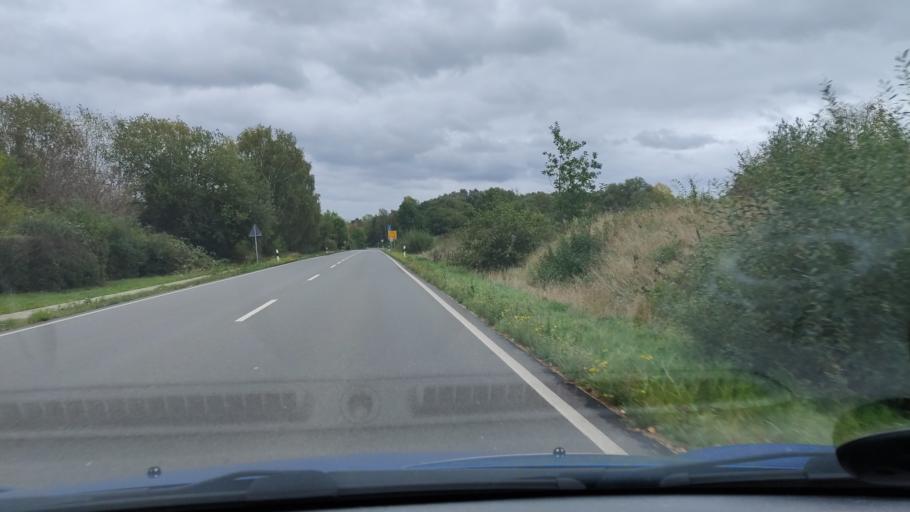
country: DE
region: Lower Saxony
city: Garbsen
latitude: 52.4045
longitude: 9.5295
